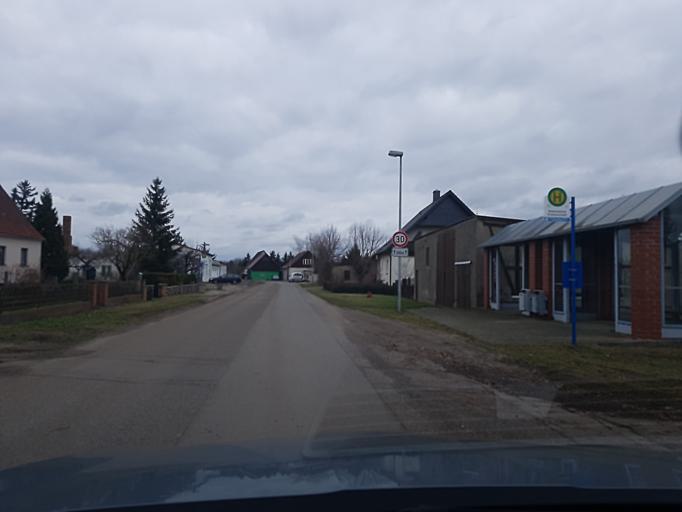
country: DE
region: Brandenburg
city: Bad Liebenwerda
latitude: 51.5491
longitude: 13.3609
